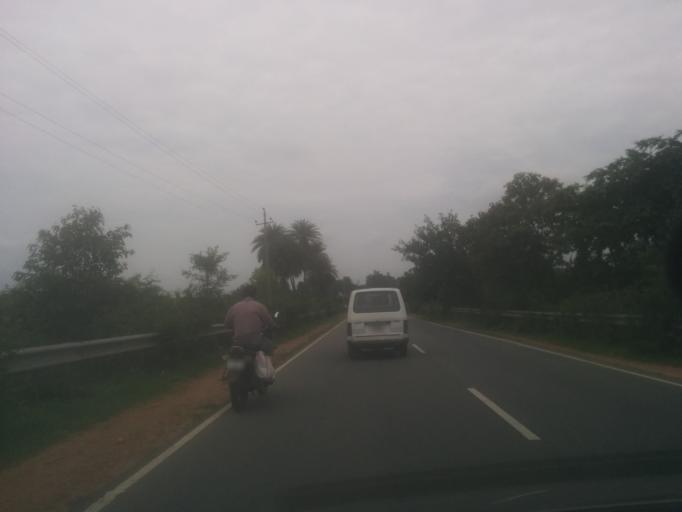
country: IN
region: Karnataka
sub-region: Hassan
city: Belur
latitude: 13.1633
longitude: 75.8867
